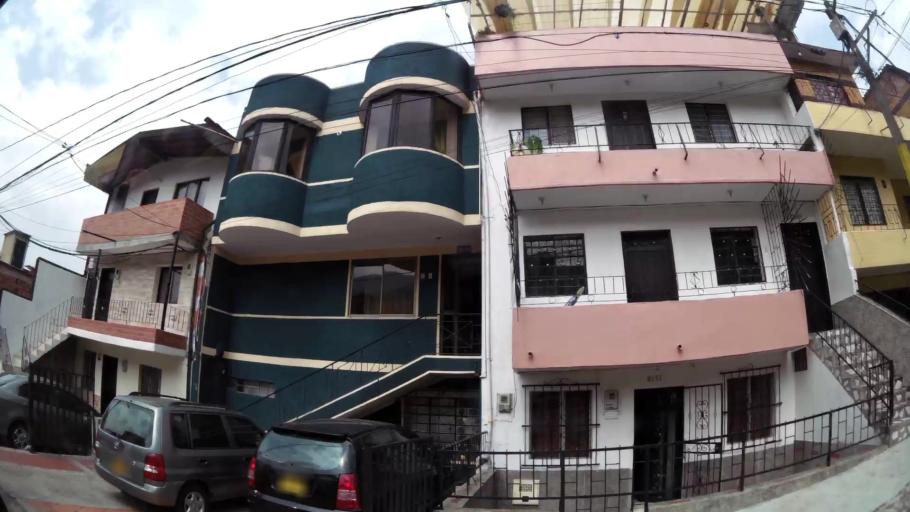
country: CO
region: Antioquia
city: Medellin
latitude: 6.2773
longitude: -75.5516
